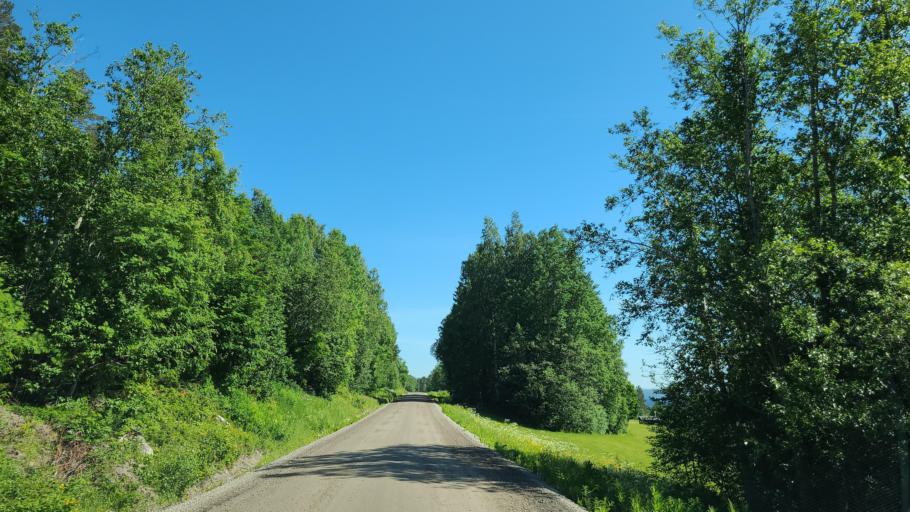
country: SE
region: Vaesterbotten
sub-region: Bjurholms Kommun
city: Bjurholm
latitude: 63.6784
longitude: 19.0038
